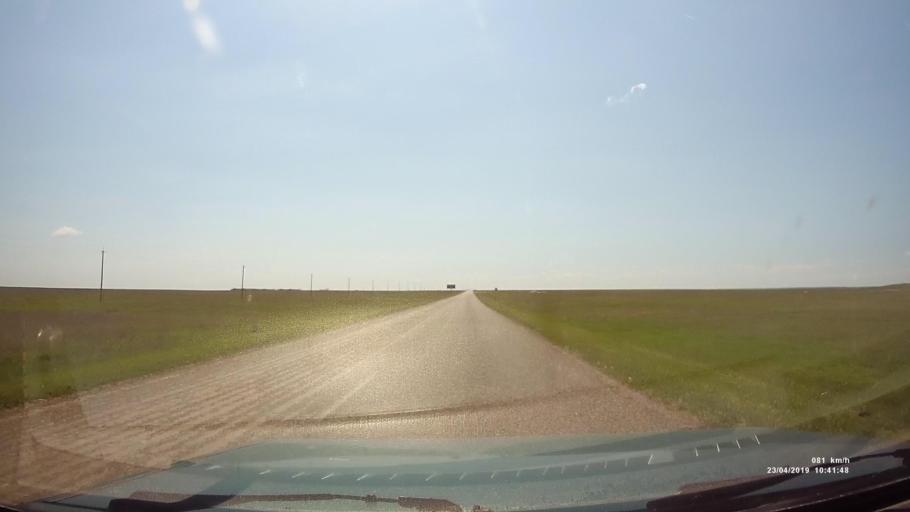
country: RU
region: Kalmykiya
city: Yashalta
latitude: 46.4900
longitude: 42.6393
